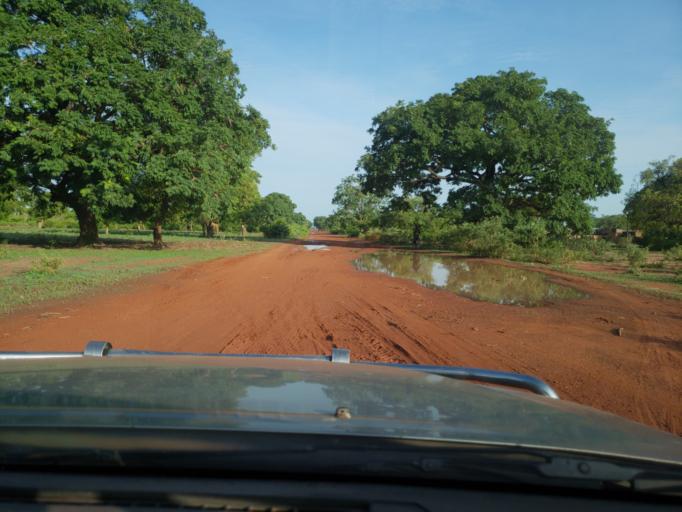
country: ML
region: Sikasso
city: Koutiala
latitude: 12.4263
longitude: -5.5975
